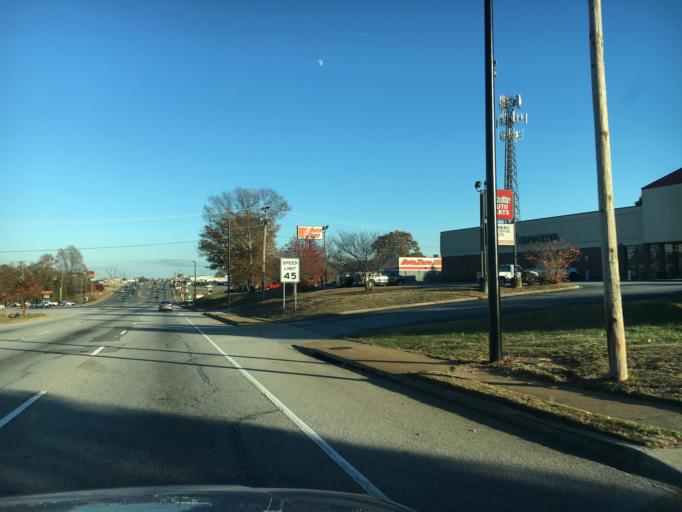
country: US
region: South Carolina
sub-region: Greenville County
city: Greer
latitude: 34.9481
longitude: -82.2239
